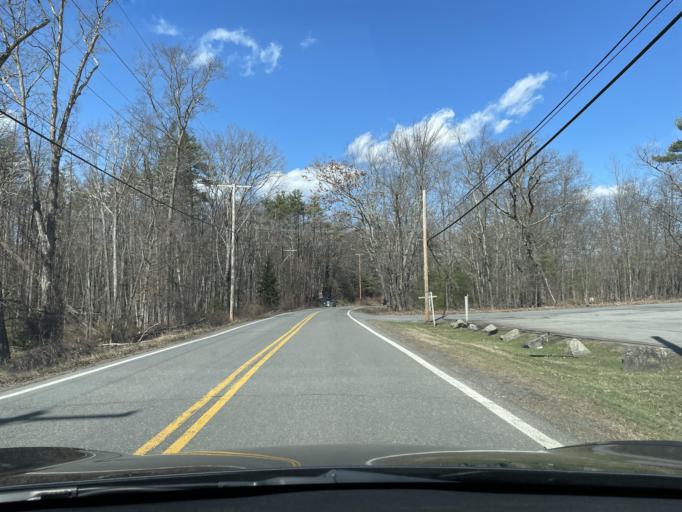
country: US
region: New York
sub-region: Ulster County
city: West Hurley
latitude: 41.9917
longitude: -74.0889
